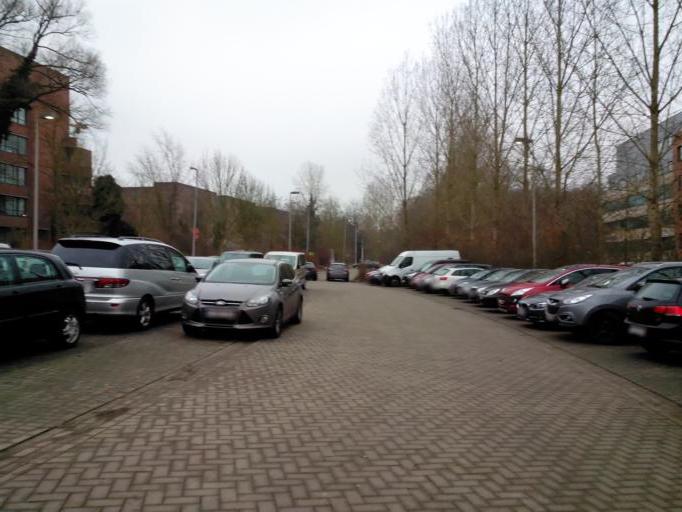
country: BE
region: Flanders
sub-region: Provincie Vlaams-Brabant
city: Leuven
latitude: 50.8644
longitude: 4.6776
